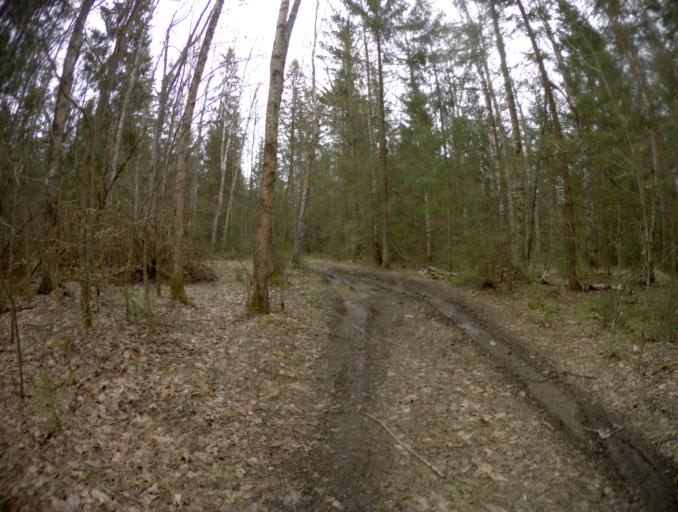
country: RU
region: Vladimir
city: Sudogda
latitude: 56.0278
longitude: 40.7945
